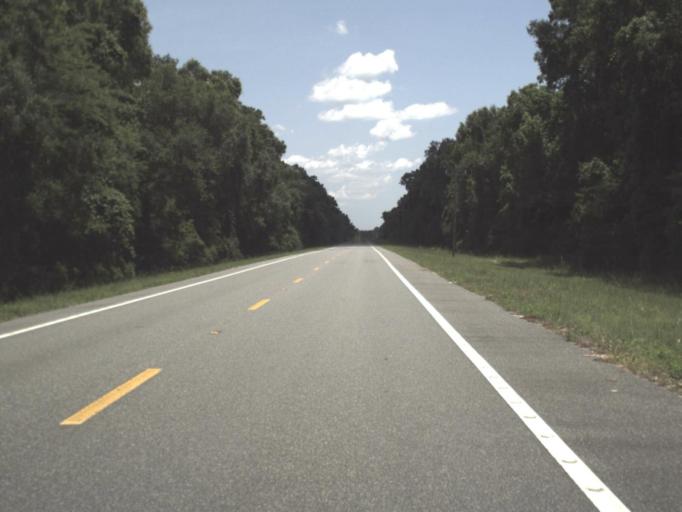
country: US
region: Florida
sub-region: Taylor County
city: Steinhatchee
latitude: 29.7464
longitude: -83.3543
